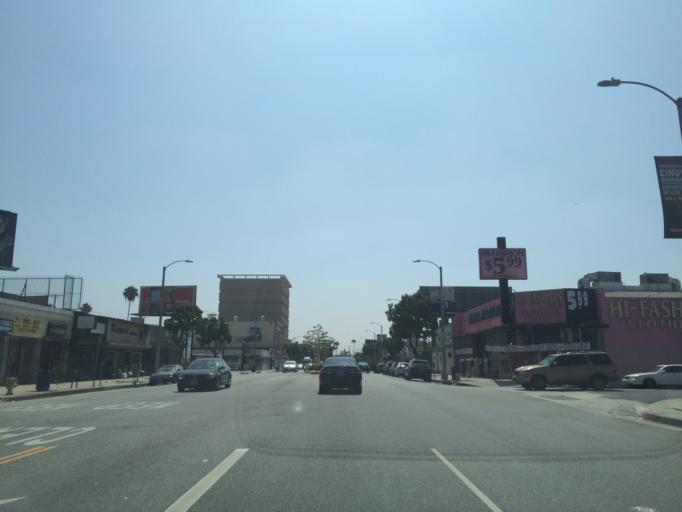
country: US
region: California
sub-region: Los Angeles County
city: West Hollywood
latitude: 34.0513
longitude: -118.3659
